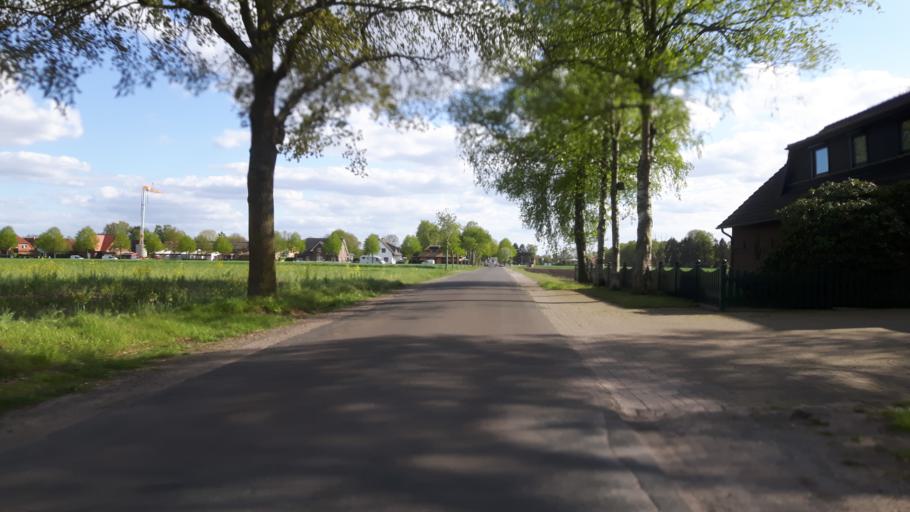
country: DE
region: Lower Saxony
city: Kirchseelte
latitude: 52.9982
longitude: 8.6889
